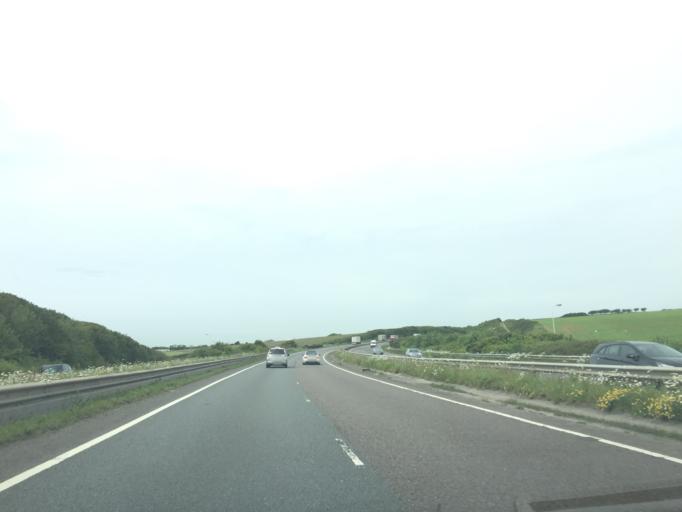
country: GB
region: England
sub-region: Kent
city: Folkestone
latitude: 51.1038
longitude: 1.2436
